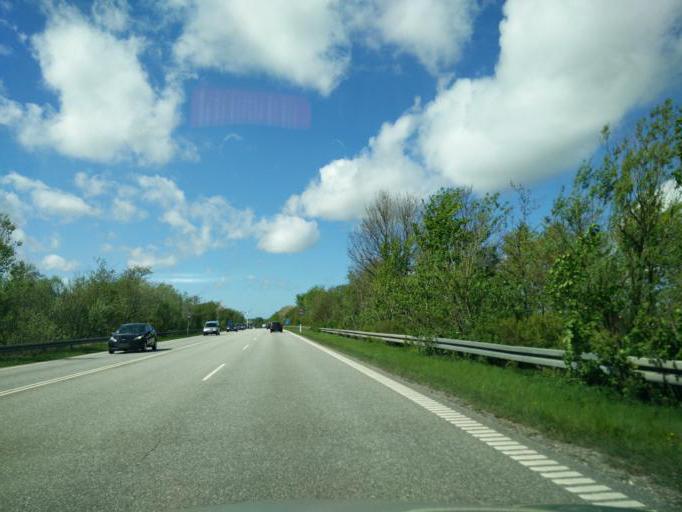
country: DK
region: Capital Region
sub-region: Hillerod Kommune
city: Hillerod
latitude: 55.8931
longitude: 12.2871
